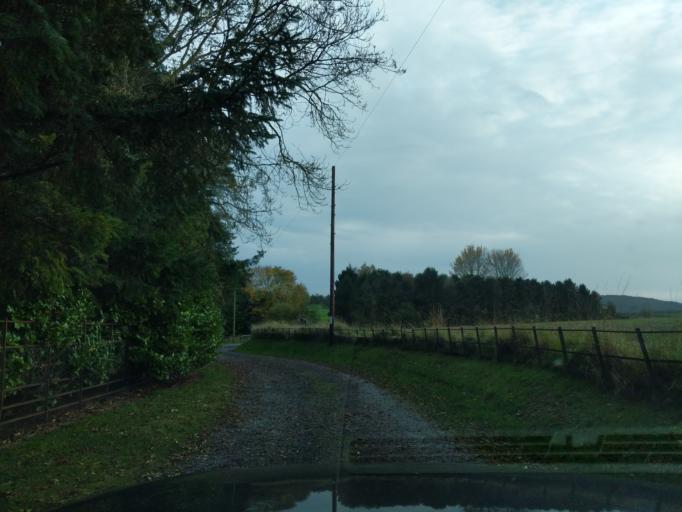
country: GB
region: Scotland
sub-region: Fife
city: Newport-On-Tay
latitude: 56.4220
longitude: -2.9138
